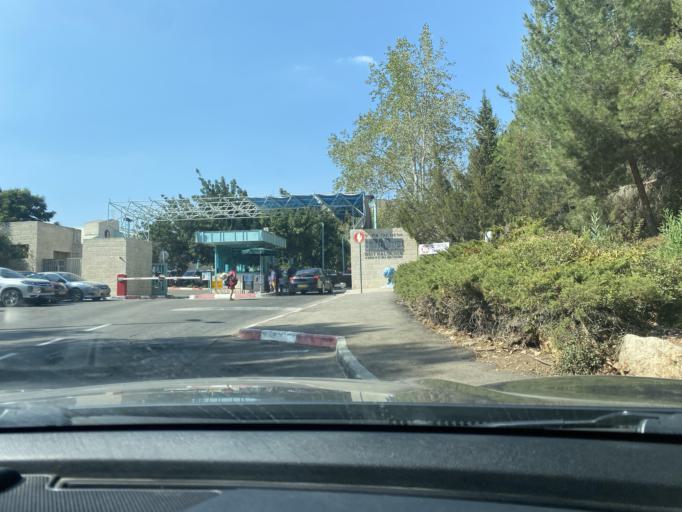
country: PS
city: Khallat Hamamah
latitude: 31.7490
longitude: 35.1779
